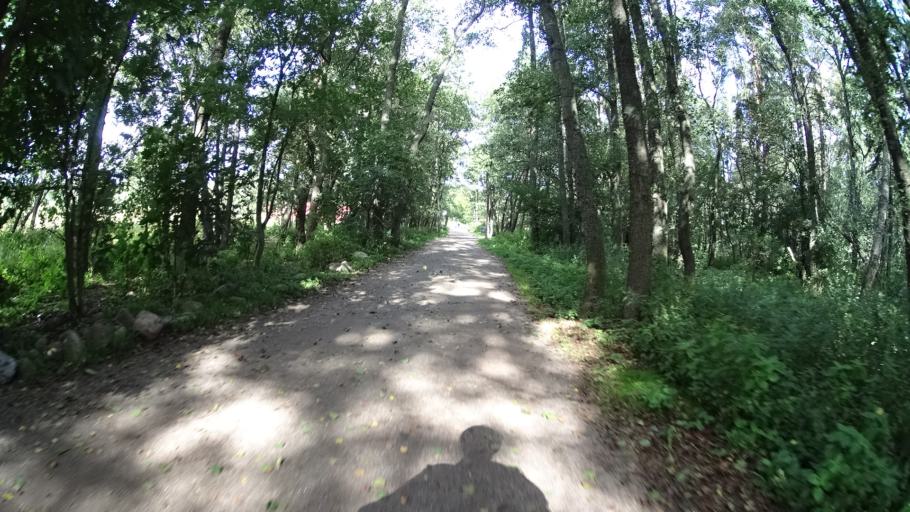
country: FI
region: Uusimaa
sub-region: Helsinki
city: Teekkarikylae
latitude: 60.1535
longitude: 24.8749
